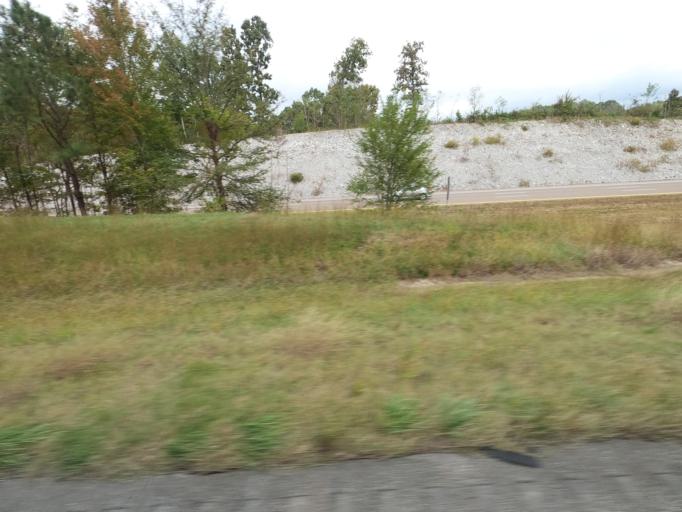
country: US
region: Tennessee
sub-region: Dickson County
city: Dickson
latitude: 35.9755
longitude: -87.5191
